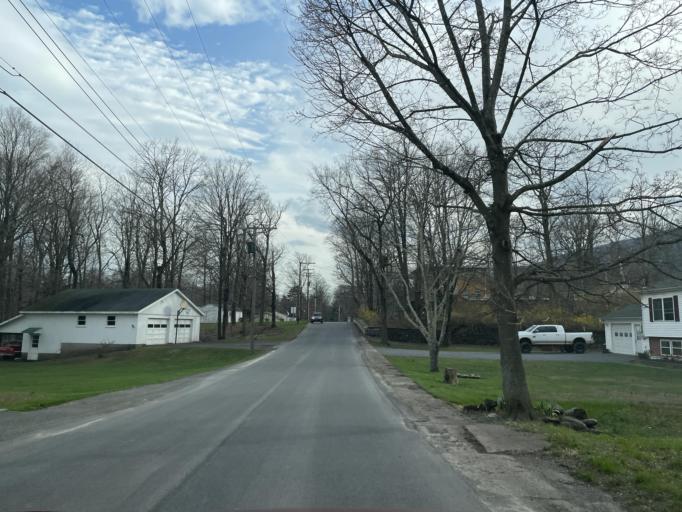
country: US
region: New York
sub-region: Greene County
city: Palenville
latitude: 42.1712
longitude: -74.0205
